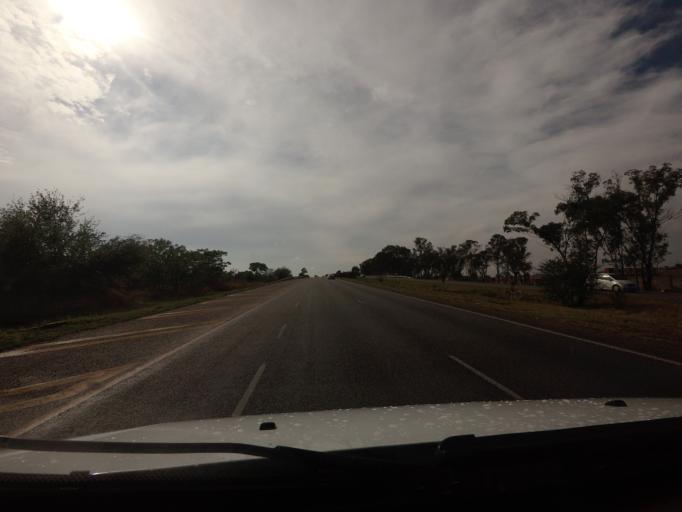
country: ZA
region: Gauteng
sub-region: City of Tshwane Metropolitan Municipality
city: Pretoria
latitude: -25.7543
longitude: 28.3396
